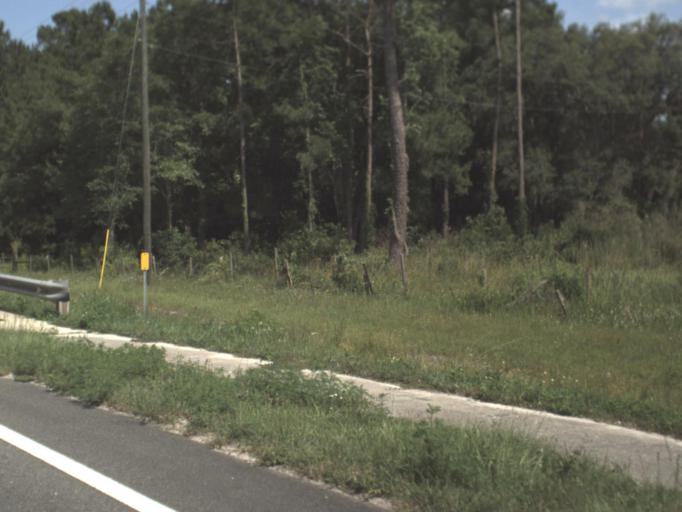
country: US
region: Florida
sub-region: Clay County
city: Asbury Lake
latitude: 29.9829
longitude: -81.7761
